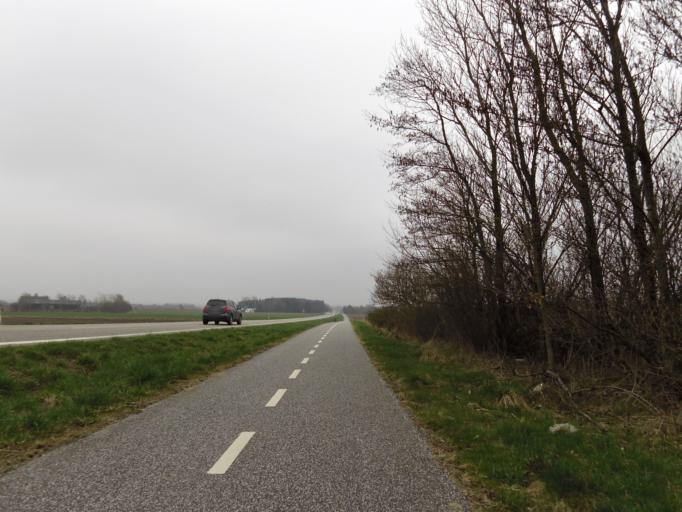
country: DK
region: Central Jutland
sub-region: Holstebro Kommune
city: Vinderup
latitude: 56.5002
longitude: 8.7952
